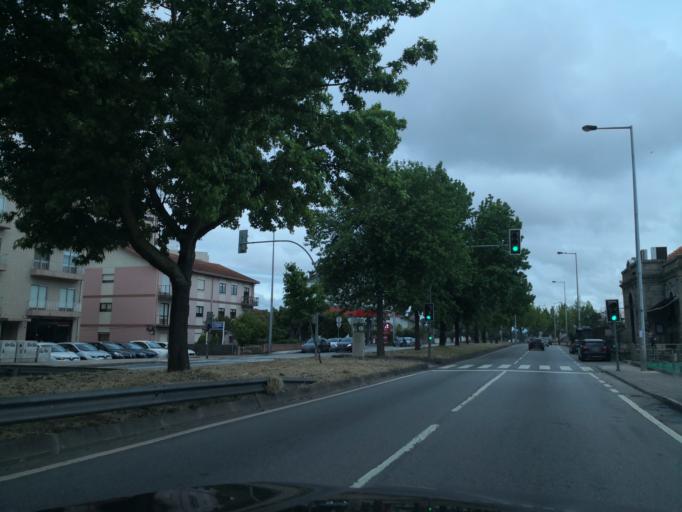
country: PT
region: Porto
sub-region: Gondomar
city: Rio Tinto
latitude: 41.1732
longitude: -8.5677
